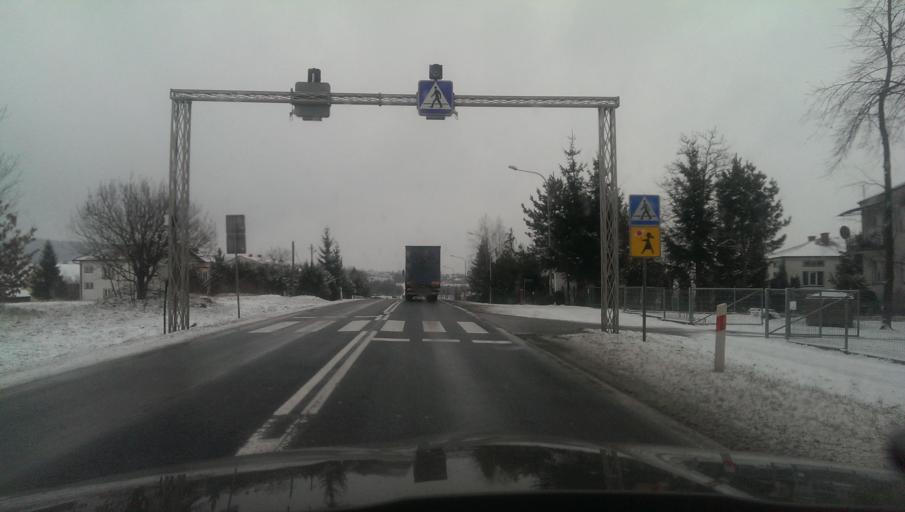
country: PL
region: Subcarpathian Voivodeship
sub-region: Powiat sanocki
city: Dlugie
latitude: 49.5765
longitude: 22.0489
